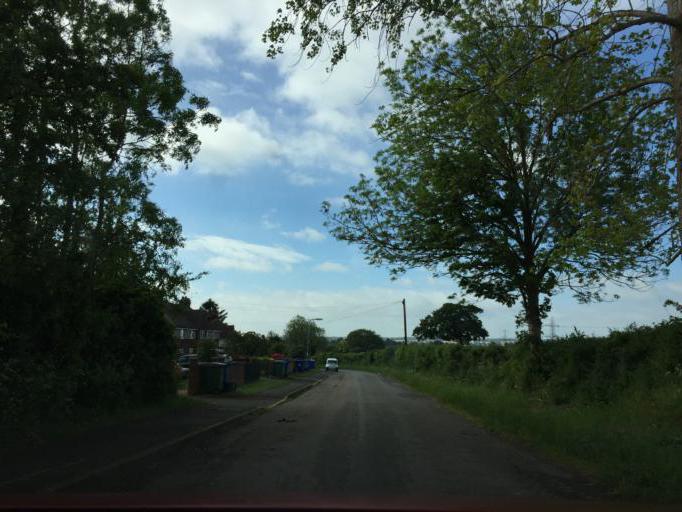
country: GB
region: England
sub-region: Northamptonshire
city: Blisworth
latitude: 52.1443
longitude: -0.9416
